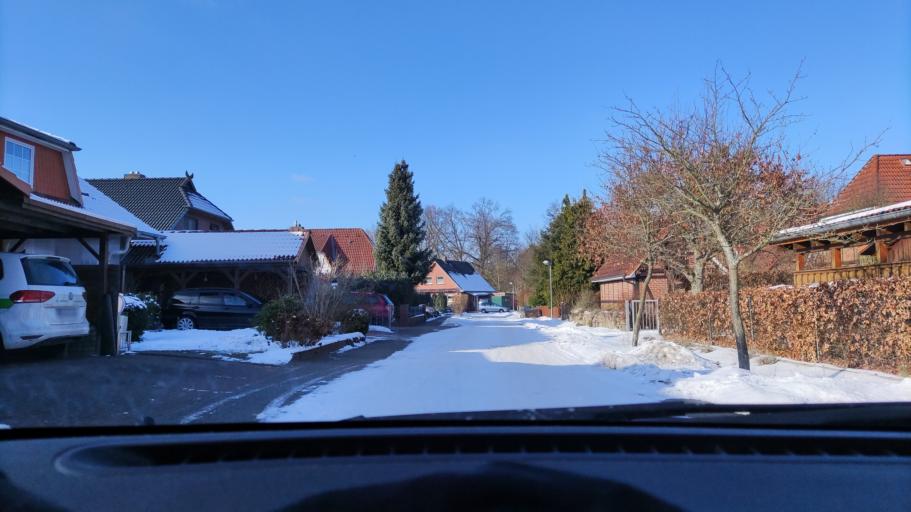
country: DE
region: Lower Saxony
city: Wendisch Evern
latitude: 53.2170
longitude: 10.4798
